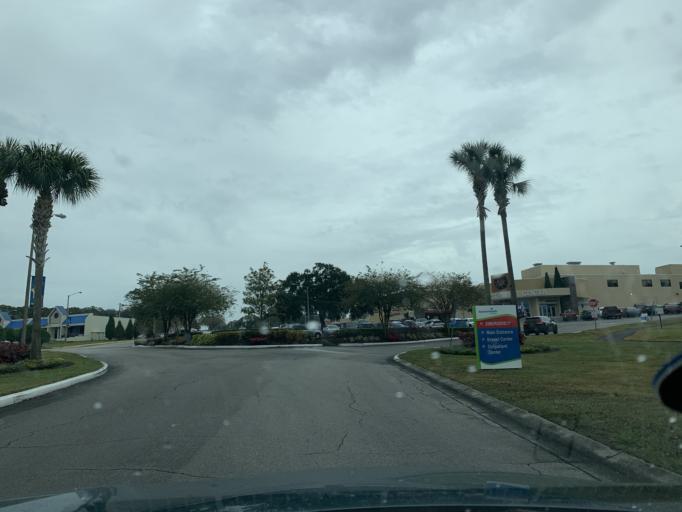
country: US
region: Florida
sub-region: Pasco County
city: Zephyrhills North
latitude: 28.2612
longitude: -82.1871
